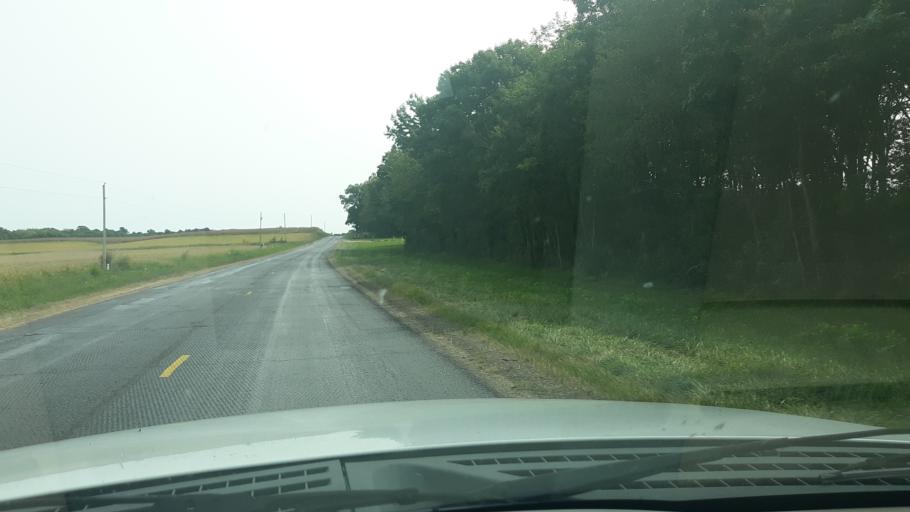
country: US
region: Illinois
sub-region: Edwards County
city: Grayville
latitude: 38.2937
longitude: -87.9684
